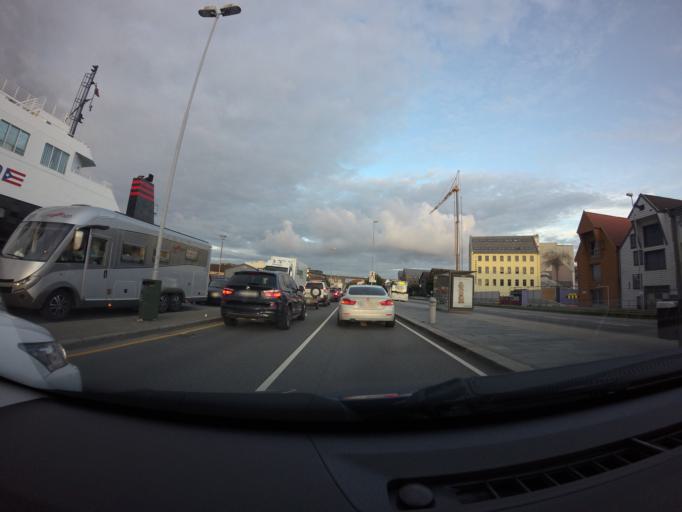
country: NO
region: Rogaland
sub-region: Stavanger
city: Stavanger
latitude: 58.9717
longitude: 5.7410
